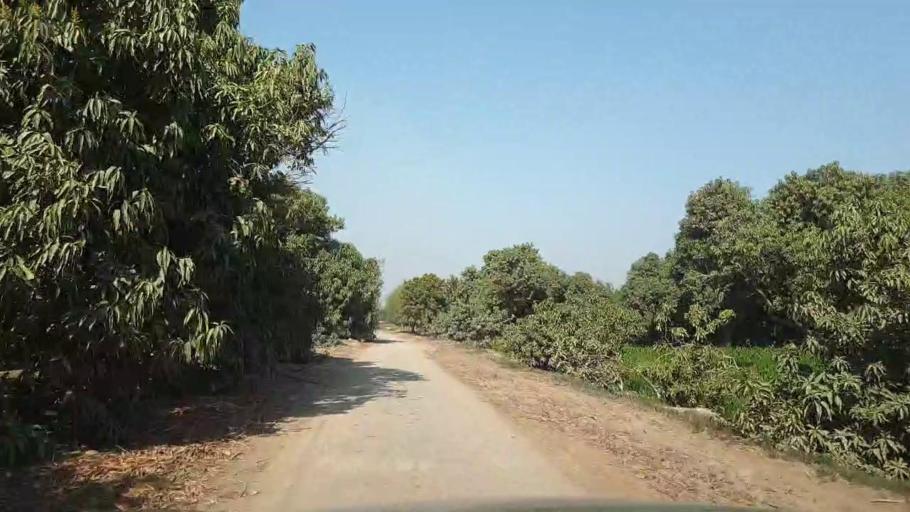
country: PK
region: Sindh
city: Tando Allahyar
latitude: 25.5589
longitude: 68.7092
